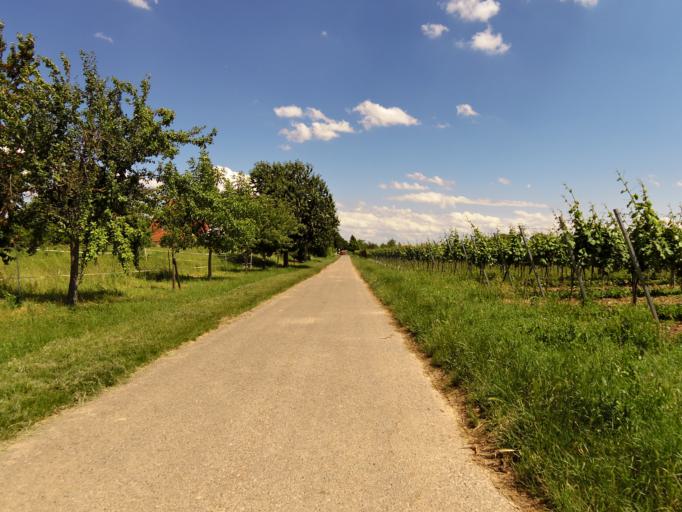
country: DE
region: Rheinland-Pfalz
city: Grossfischlingen
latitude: 49.2673
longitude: 8.1709
